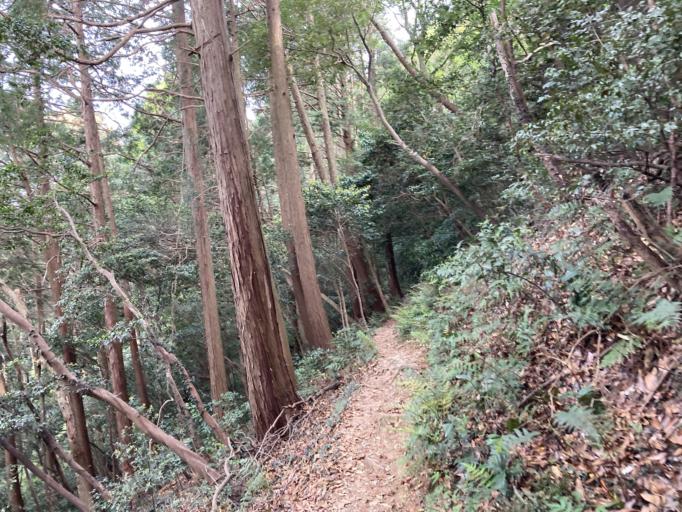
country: JP
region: Shizuoka
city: Kosai-shi
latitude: 34.7446
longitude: 137.4649
